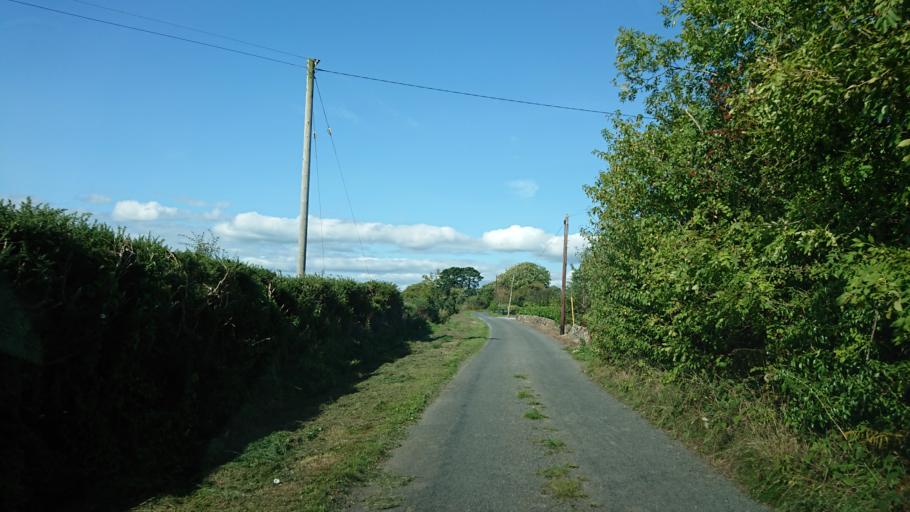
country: IE
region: Munster
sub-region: Waterford
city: Waterford
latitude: 52.2147
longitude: -7.0540
